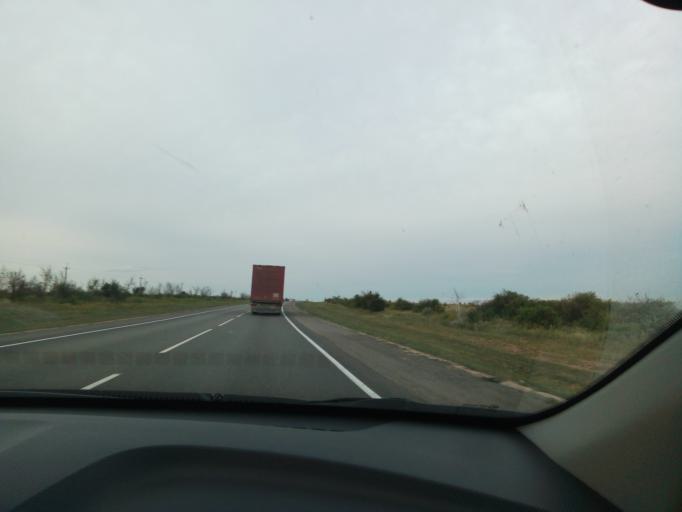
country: RU
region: Volgograd
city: Dubovka
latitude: 49.1500
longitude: 44.8350
